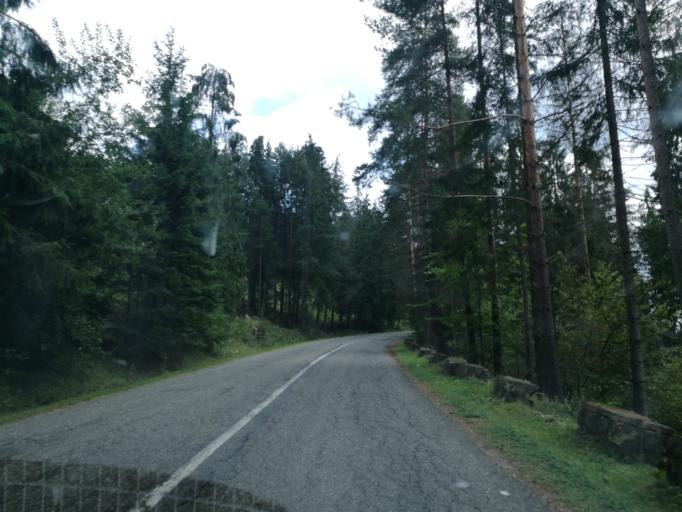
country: RO
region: Suceava
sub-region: Comuna Moldovita
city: Moldovita
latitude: 47.7280
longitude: 25.6085
